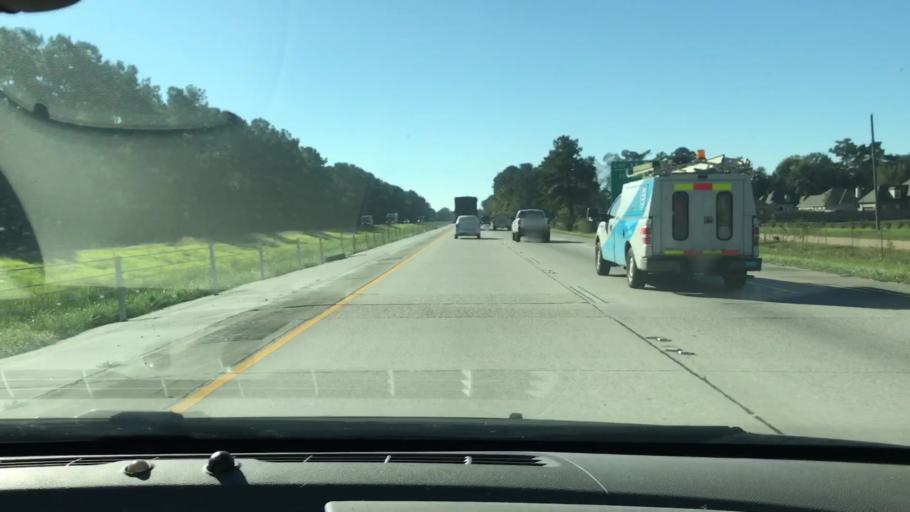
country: US
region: Louisiana
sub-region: Saint Tammany Parish
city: Pearl River
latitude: 30.3320
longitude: -89.7379
